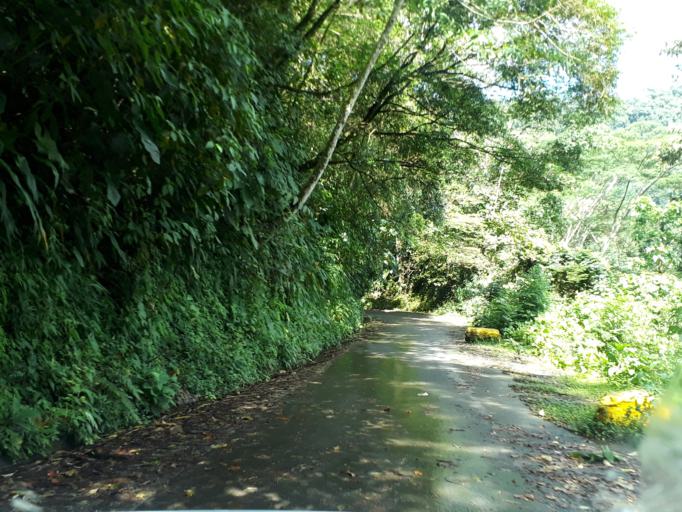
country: CO
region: Boyaca
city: Santa Maria
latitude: 4.7409
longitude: -73.3427
